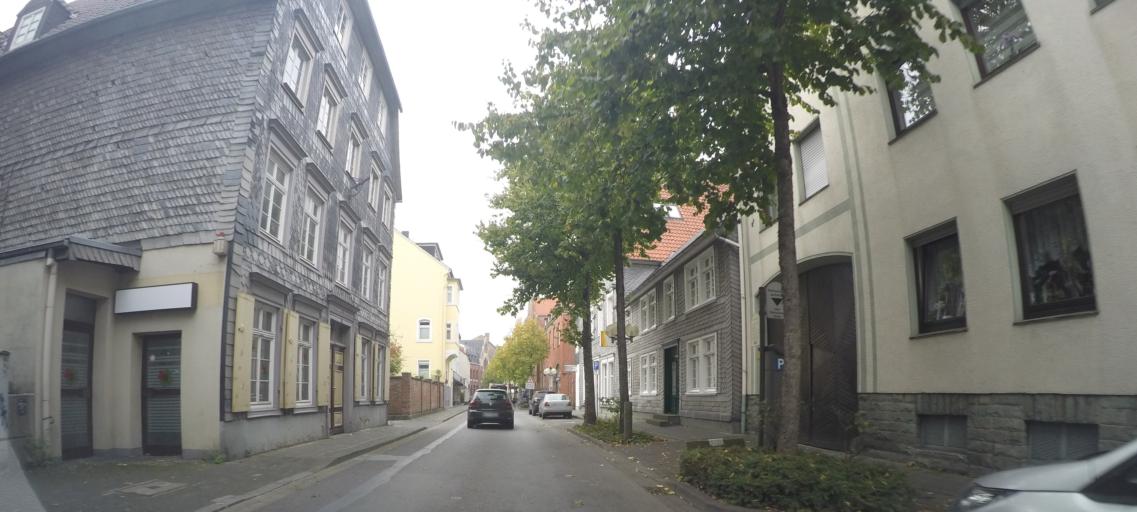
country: DE
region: North Rhine-Westphalia
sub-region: Regierungsbezirk Arnsberg
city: Lippstadt
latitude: 51.6738
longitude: 8.3486
